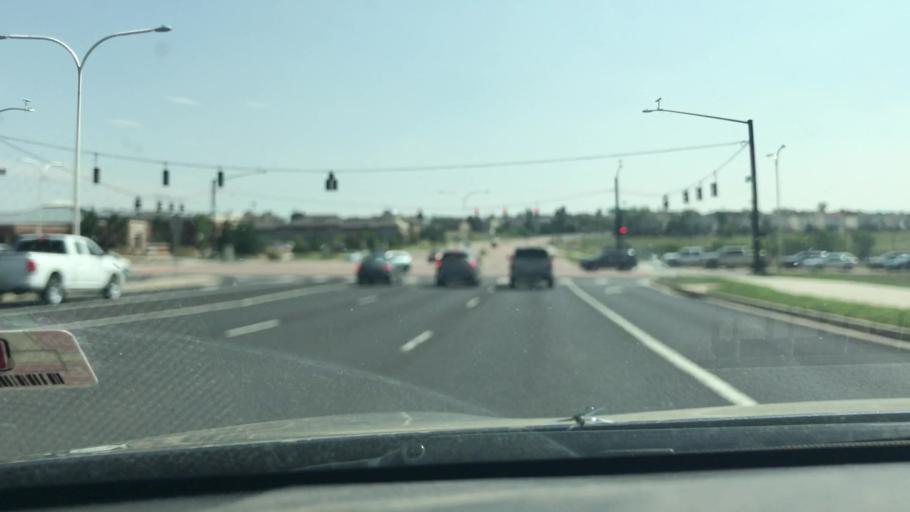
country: US
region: Colorado
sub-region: El Paso County
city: Black Forest
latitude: 38.9665
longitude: -104.7578
